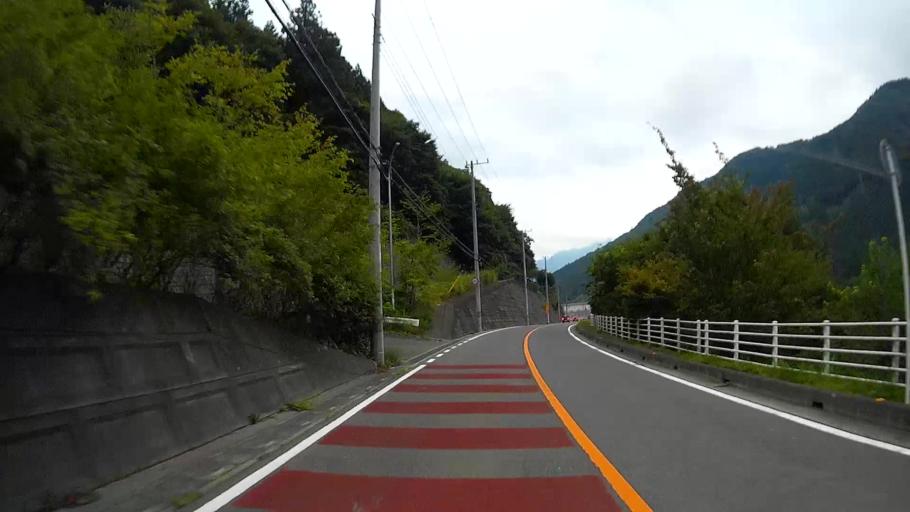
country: JP
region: Saitama
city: Chichibu
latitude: 35.9576
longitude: 138.8894
